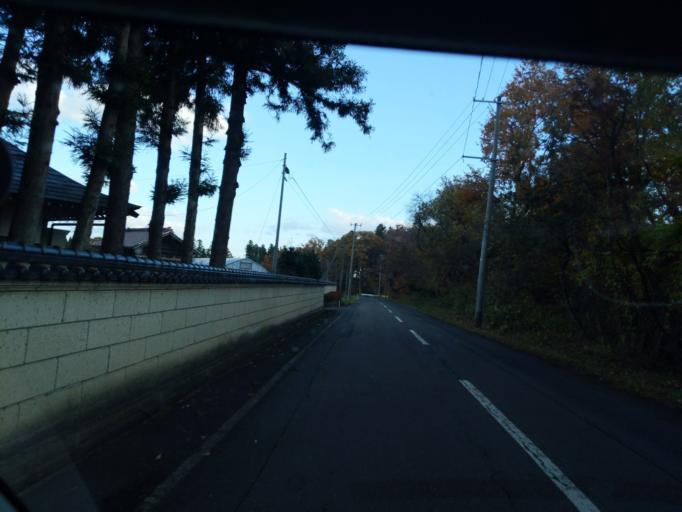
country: JP
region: Iwate
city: Mizusawa
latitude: 39.0785
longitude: 141.0429
